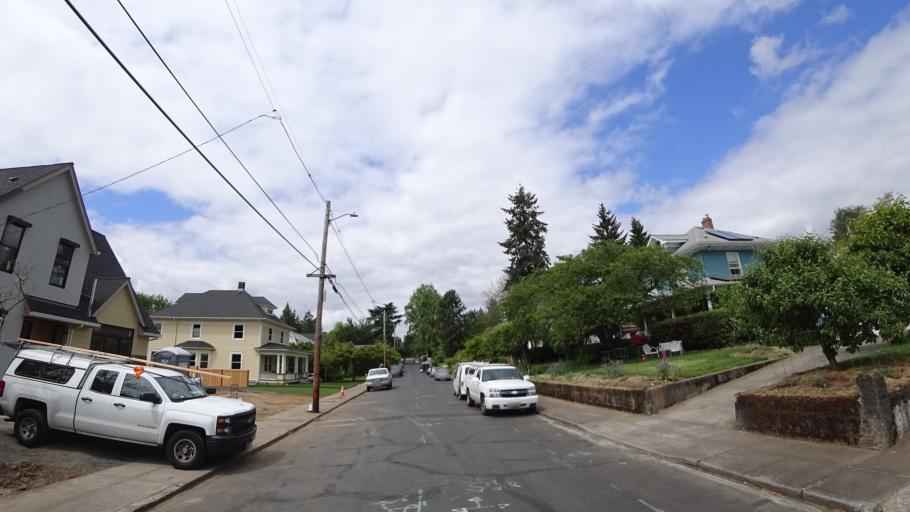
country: US
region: Oregon
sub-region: Multnomah County
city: Lents
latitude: 45.5100
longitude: -122.6045
